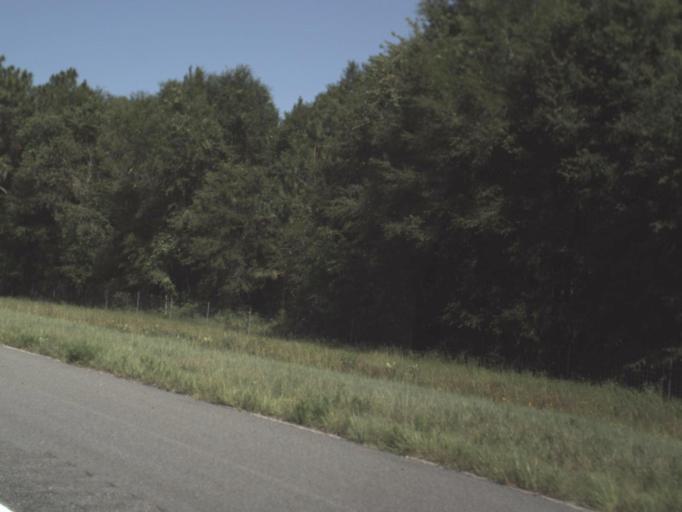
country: US
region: Florida
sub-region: Suwannee County
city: Live Oak
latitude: 30.3487
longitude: -83.0806
